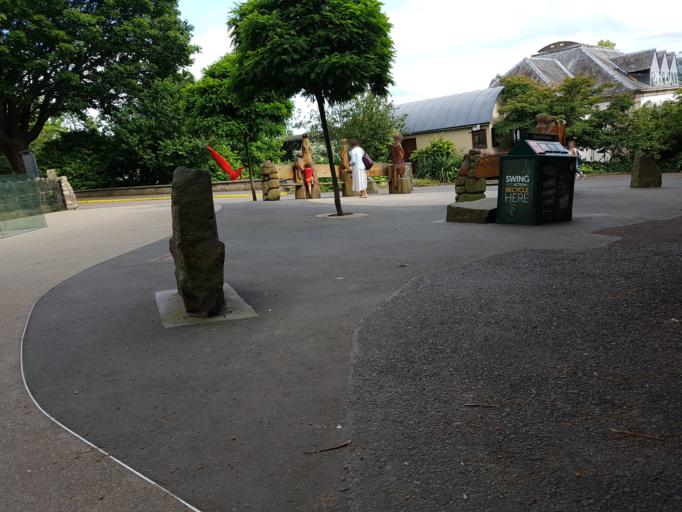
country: GB
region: Scotland
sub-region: Edinburgh
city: Colinton
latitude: 55.9425
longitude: -3.2691
